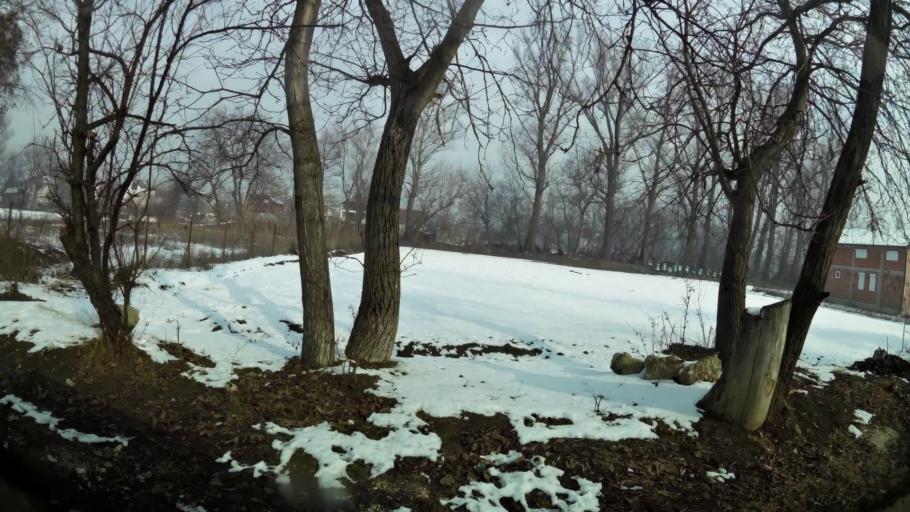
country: MK
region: Saraj
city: Saraj
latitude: 42.0258
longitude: 21.3560
